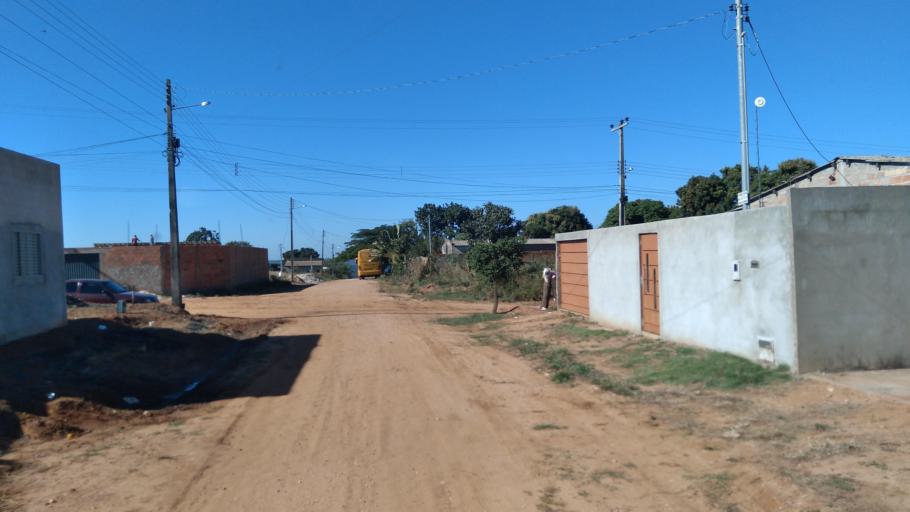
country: BR
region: Goias
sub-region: Mineiros
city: Mineiros
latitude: -17.5923
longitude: -52.5566
